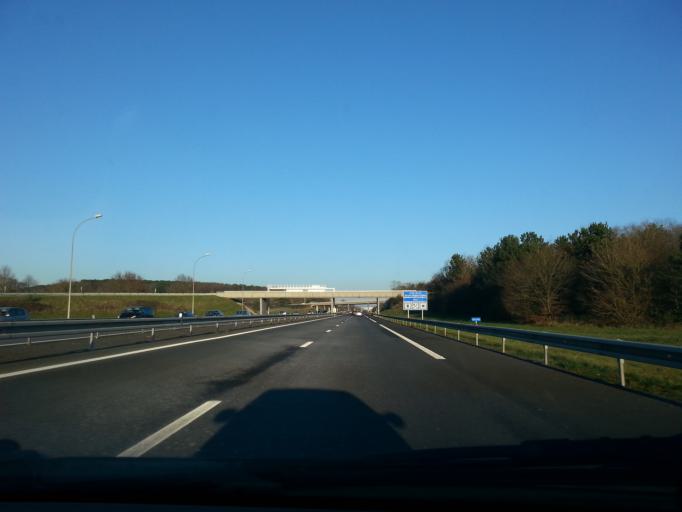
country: FR
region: Pays de la Loire
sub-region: Departement de la Sarthe
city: La Chapelle-Saint-Aubin
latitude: 48.0398
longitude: 0.1466
